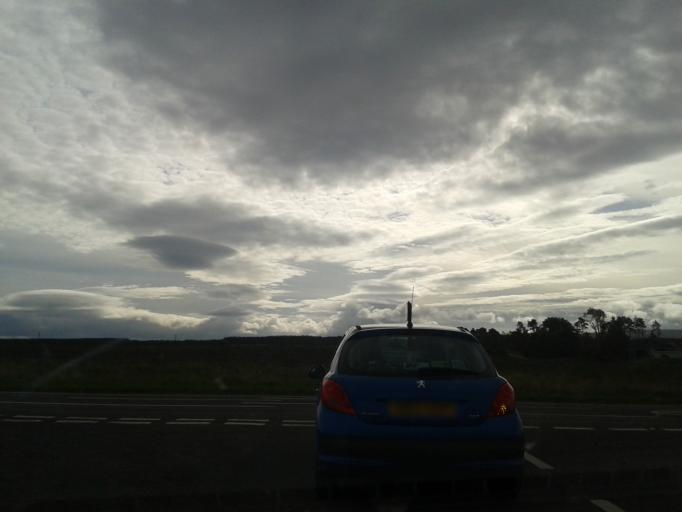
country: GB
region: Scotland
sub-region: Highland
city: Nairn
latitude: 57.5456
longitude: -4.0022
